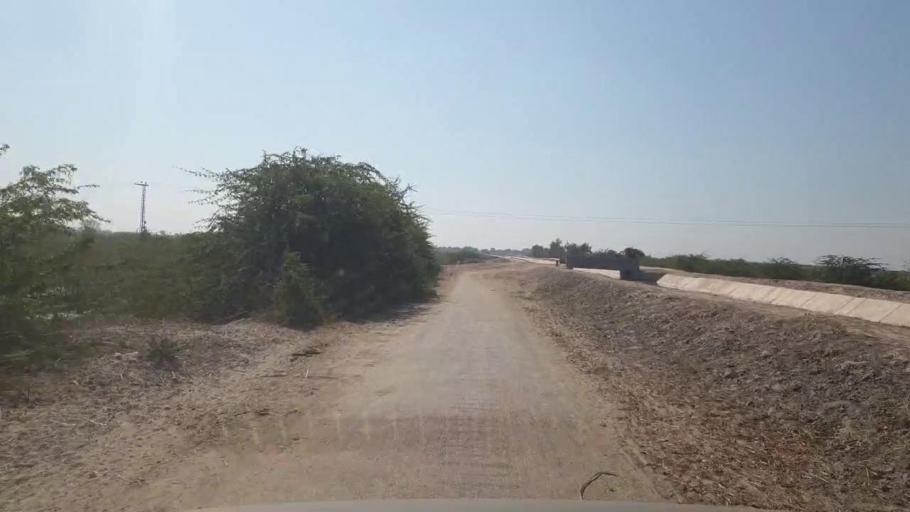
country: PK
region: Sindh
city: Mirwah Gorchani
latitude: 25.2711
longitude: 69.1039
